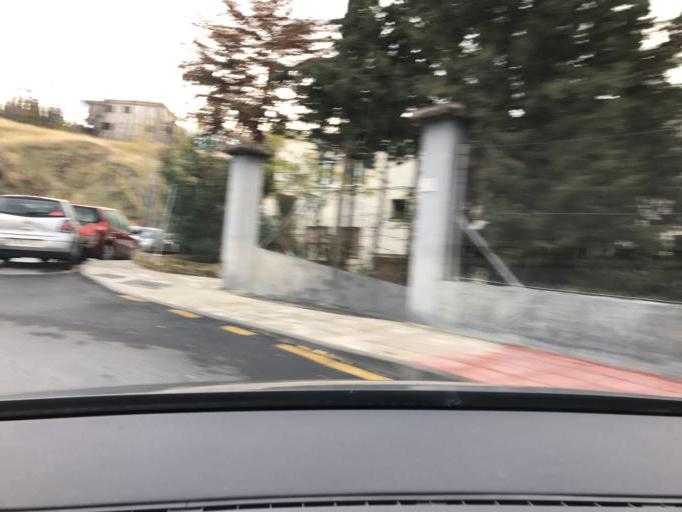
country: ES
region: Andalusia
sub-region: Provincia de Granada
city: Cenes de la Vega
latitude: 37.1615
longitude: -3.5400
